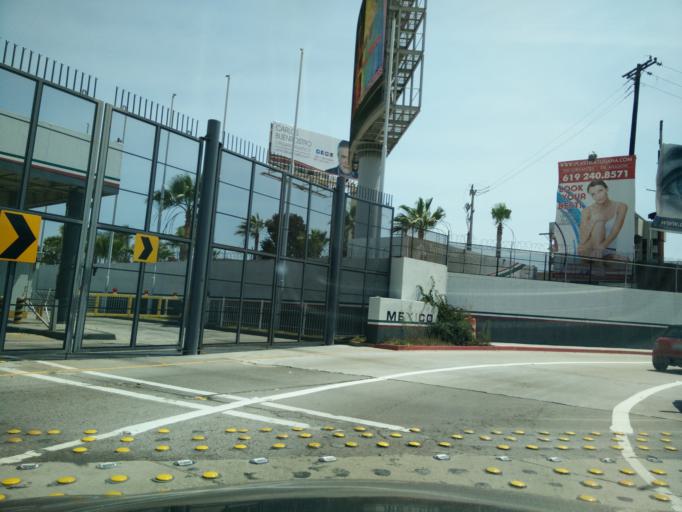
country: MX
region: Baja California
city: Tijuana
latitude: 32.5425
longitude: -117.0302
